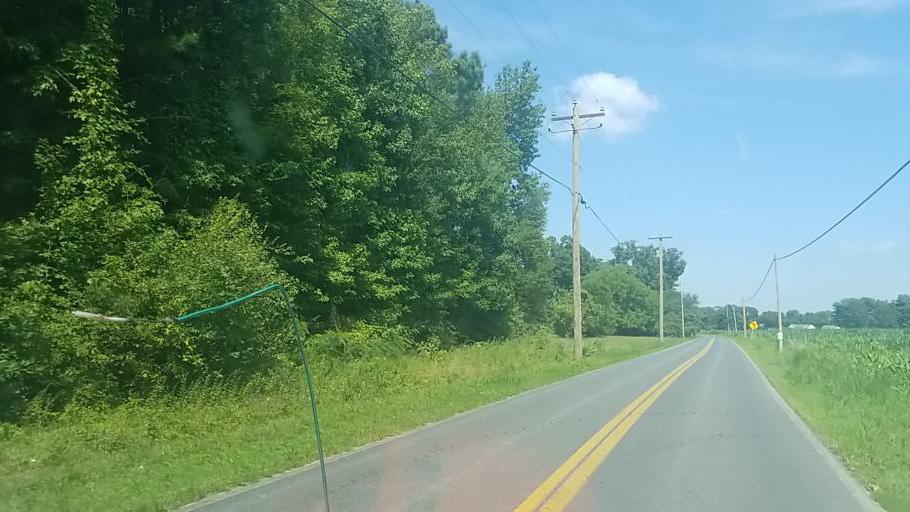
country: US
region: Maryland
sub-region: Caroline County
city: Denton
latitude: 38.8817
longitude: -75.7979
